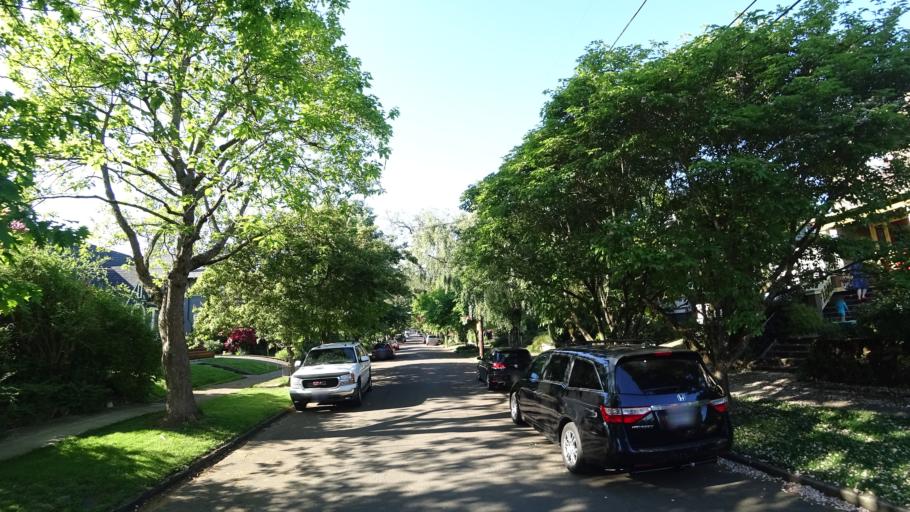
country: US
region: Oregon
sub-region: Multnomah County
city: Portland
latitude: 45.5523
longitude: -122.6841
